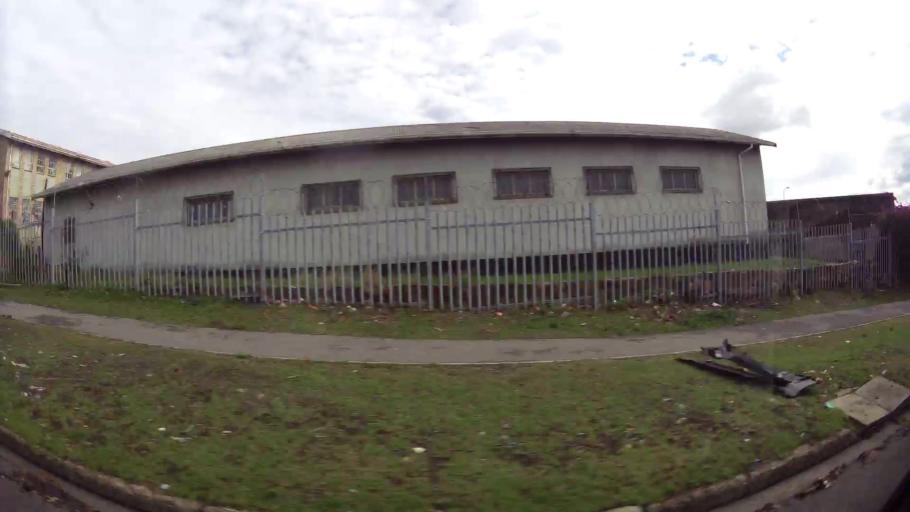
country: ZA
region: Eastern Cape
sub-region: Nelson Mandela Bay Metropolitan Municipality
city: Port Elizabeth
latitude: -33.9362
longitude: 25.5743
